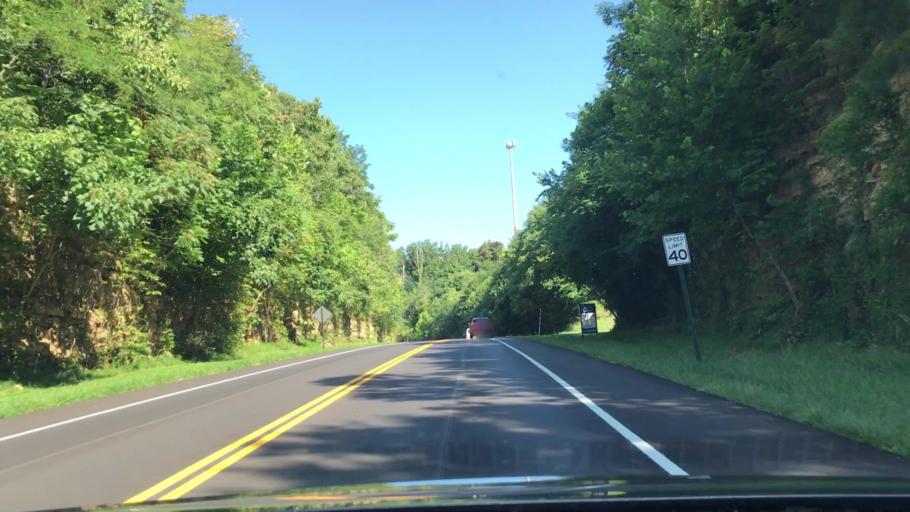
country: US
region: Tennessee
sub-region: Williamson County
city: Franklin
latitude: 35.9802
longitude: -86.8426
